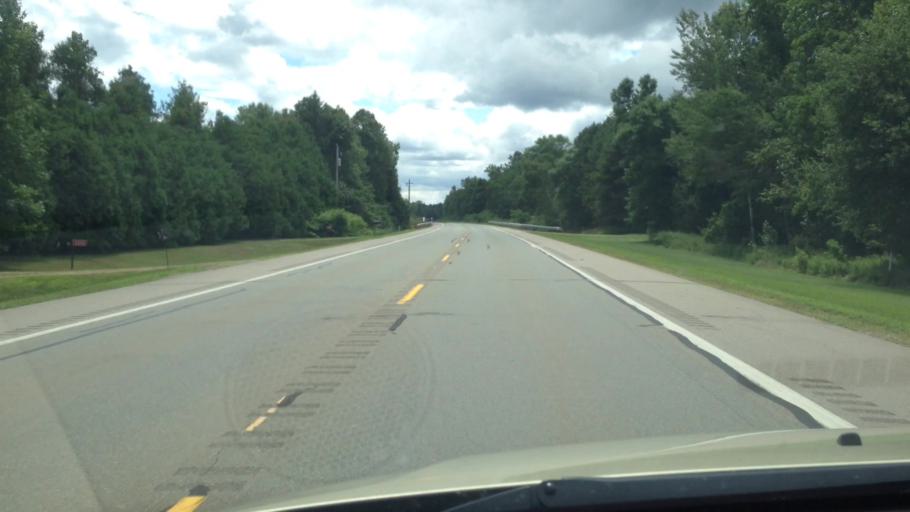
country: US
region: Michigan
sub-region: Menominee County
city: Menominee
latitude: 45.2286
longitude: -87.5108
